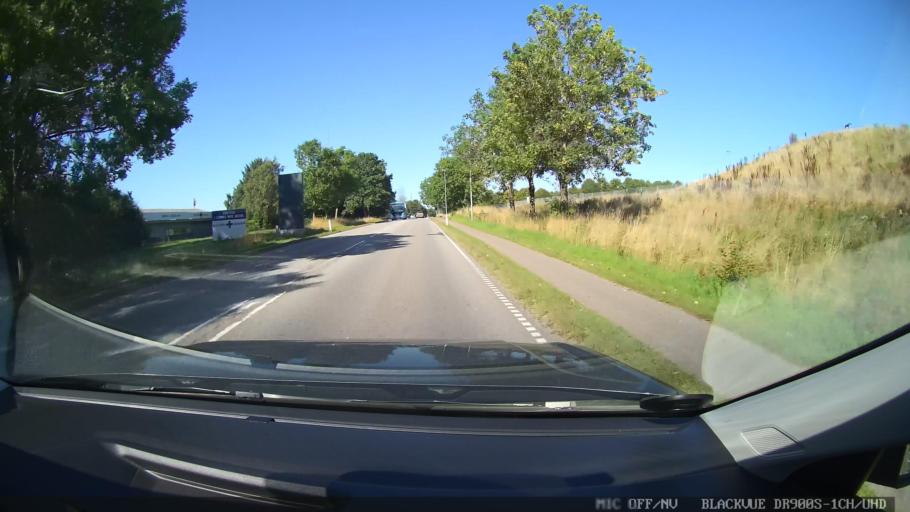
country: DK
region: Central Jutland
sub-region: Randers Kommune
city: Randers
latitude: 56.4931
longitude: 10.0249
